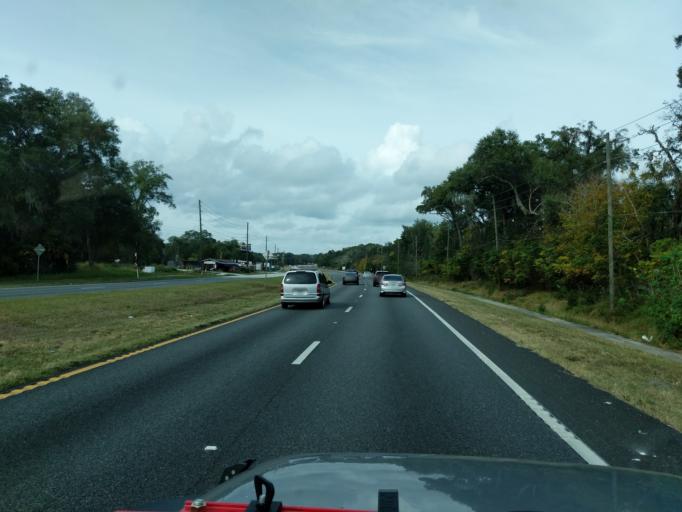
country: US
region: Florida
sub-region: Orange County
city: Zellwood
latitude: 28.7325
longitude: -81.6078
